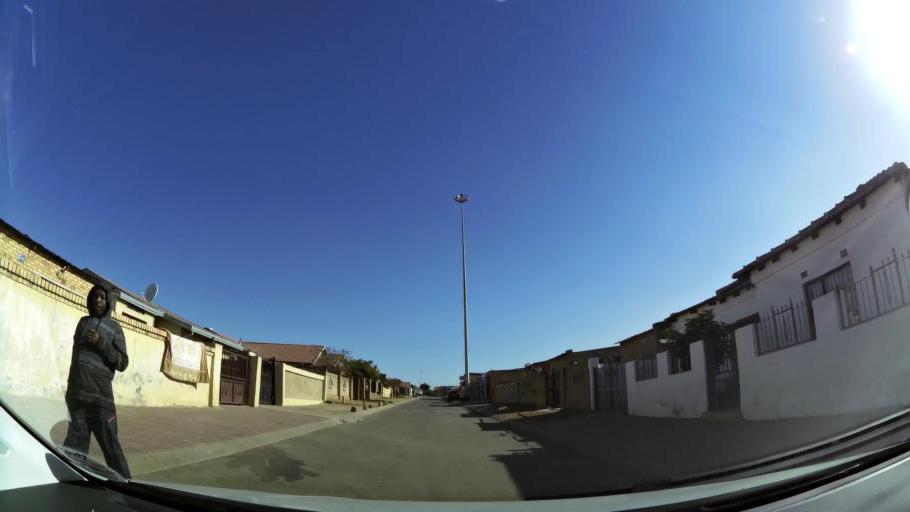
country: ZA
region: Gauteng
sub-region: Ekurhuleni Metropolitan Municipality
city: Tembisa
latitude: -26.0197
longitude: 28.2363
